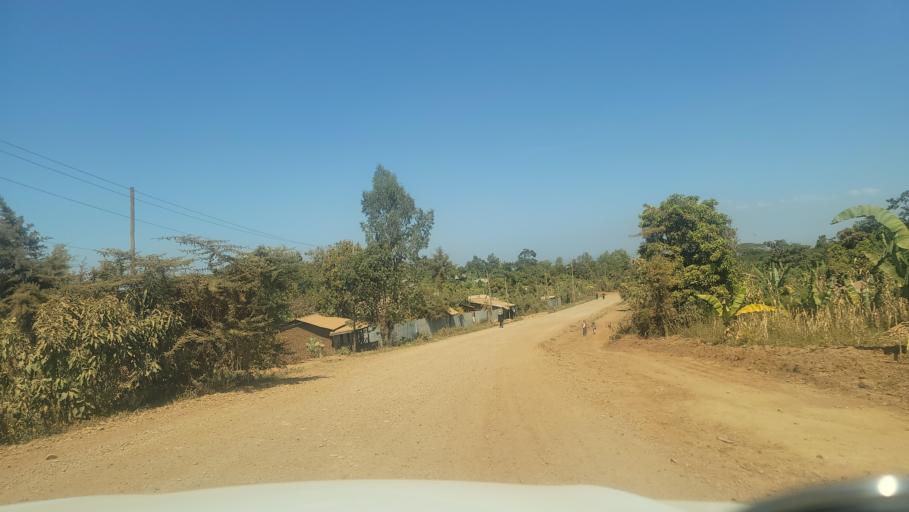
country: ET
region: Oromiya
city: Agaro
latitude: 7.8214
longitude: 36.5283
